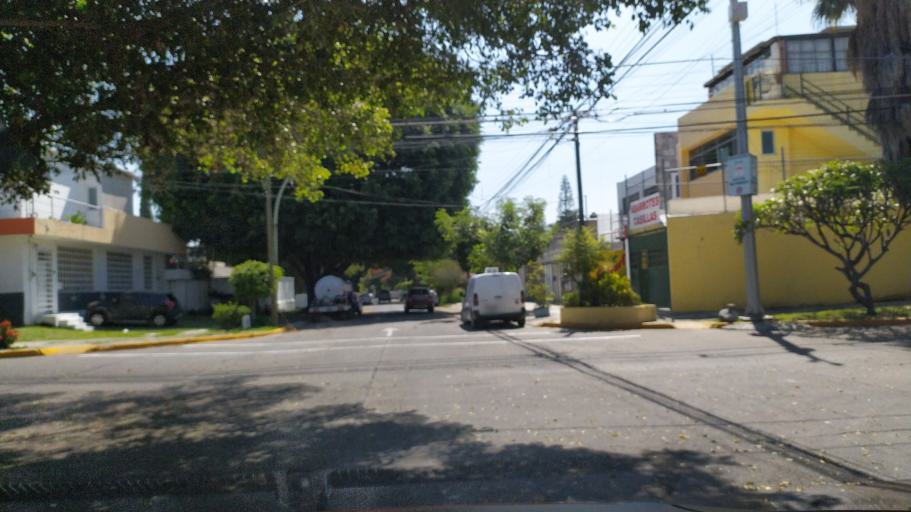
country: MX
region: Jalisco
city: Guadalajara
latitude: 20.6604
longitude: -103.4010
